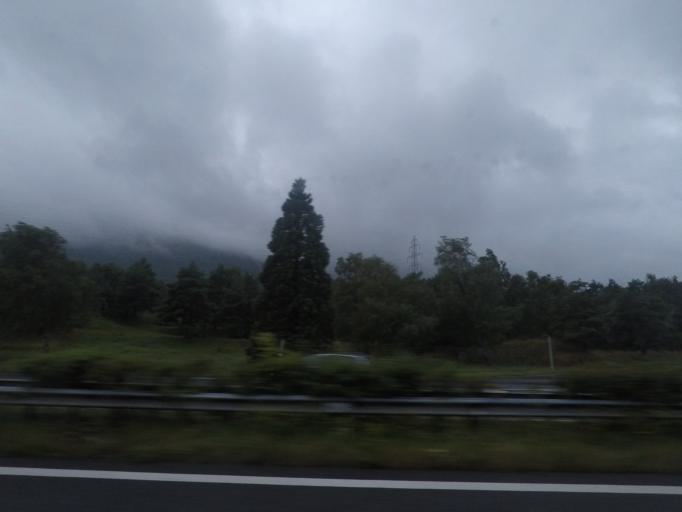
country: CH
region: Valais
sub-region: Martigny District
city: Evionnaz
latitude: 46.1835
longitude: 7.0262
